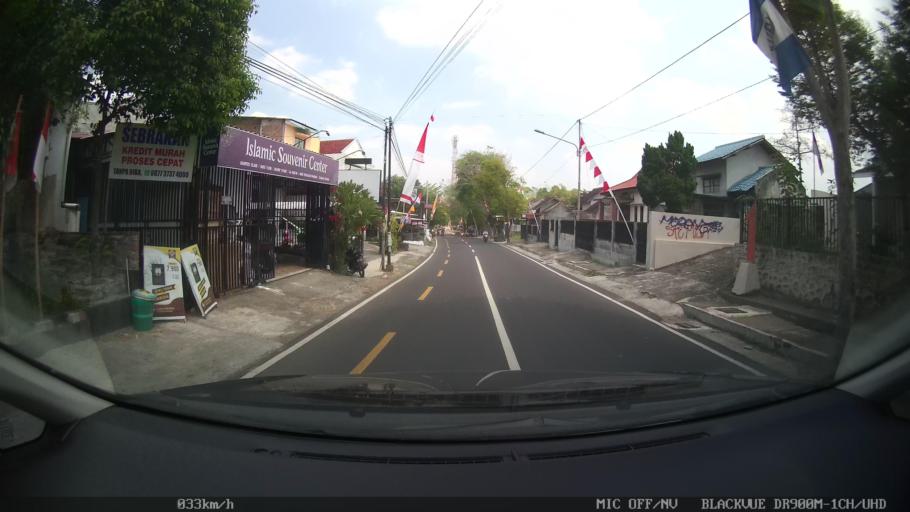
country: ID
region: Daerah Istimewa Yogyakarta
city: Yogyakarta
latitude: -7.8135
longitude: 110.3948
